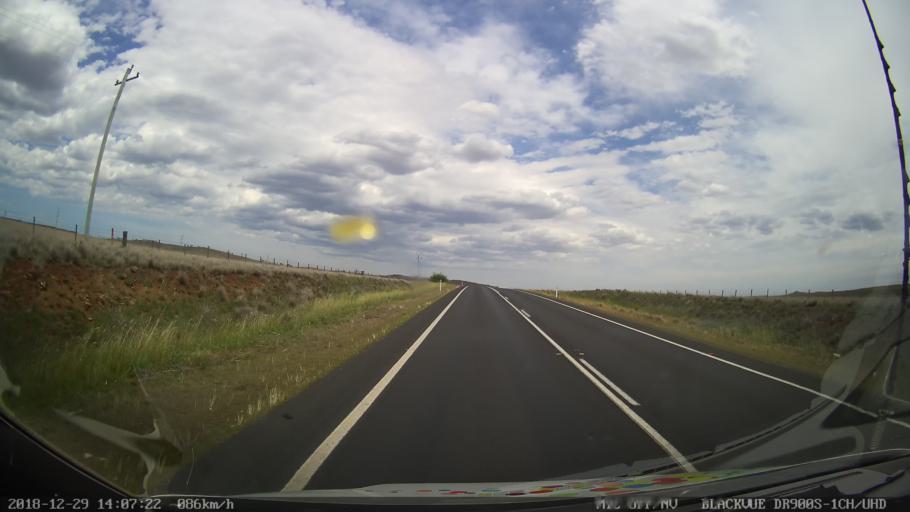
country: AU
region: New South Wales
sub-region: Cooma-Monaro
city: Cooma
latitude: -36.3509
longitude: 149.2133
